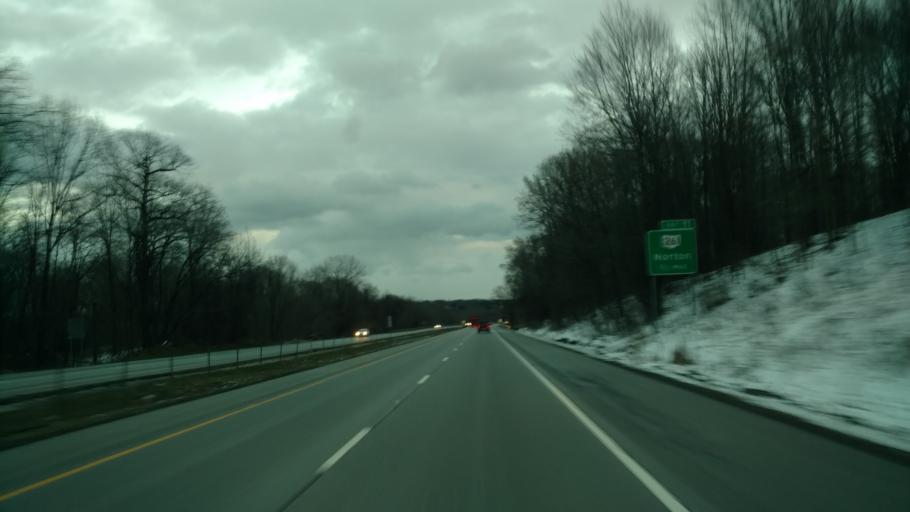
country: US
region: Ohio
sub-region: Medina County
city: Wadsworth
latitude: 41.0471
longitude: -81.7048
